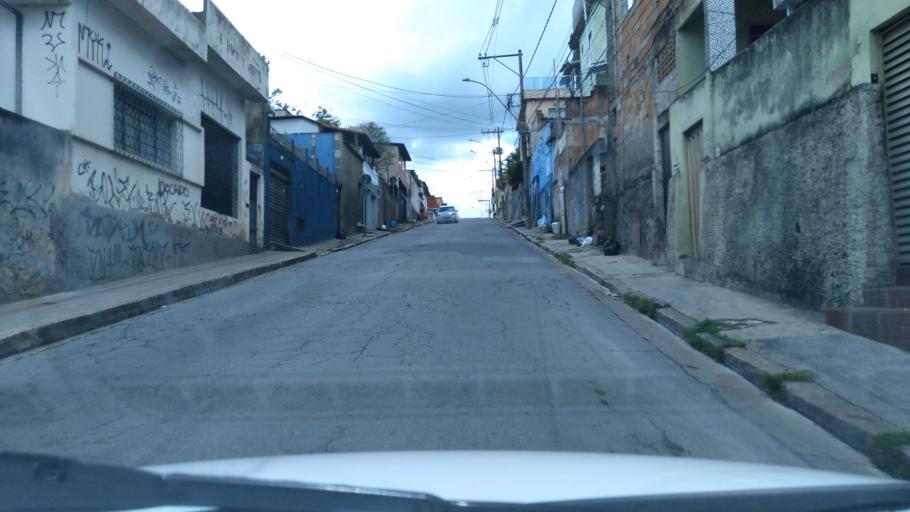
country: BR
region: Minas Gerais
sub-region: Belo Horizonte
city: Belo Horizonte
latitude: -19.9110
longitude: -43.8978
